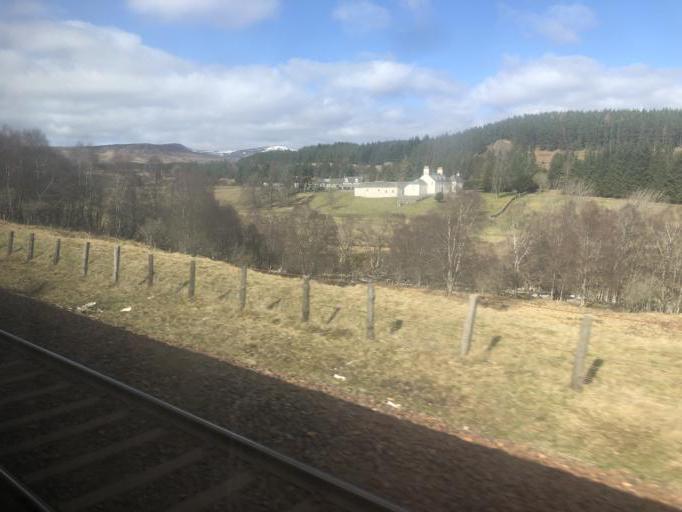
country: GB
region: Scotland
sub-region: Highland
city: Kingussie
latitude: 56.8038
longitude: -4.0938
